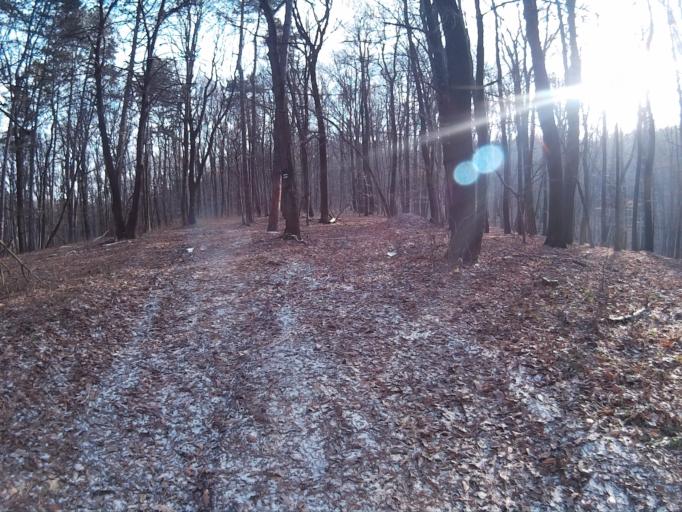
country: HU
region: Fejer
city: Szarliget
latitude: 47.4902
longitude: 18.4096
